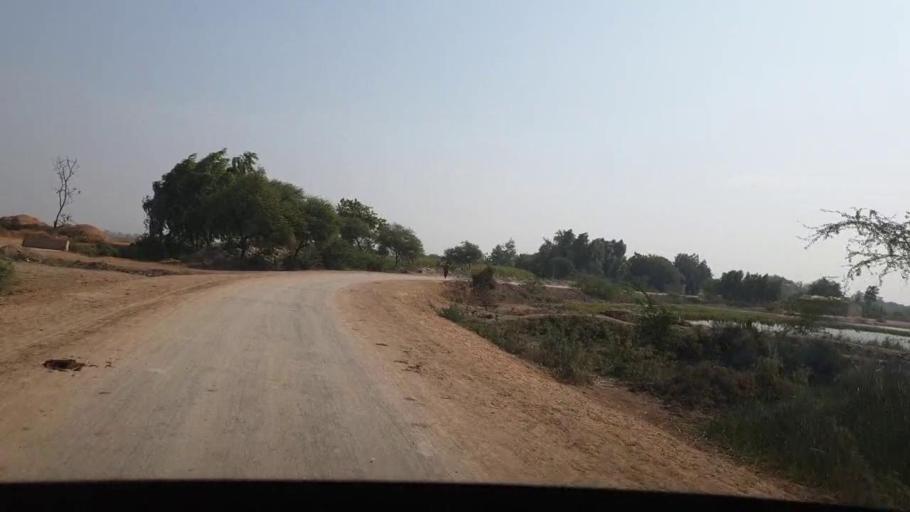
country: PK
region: Sindh
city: Chuhar Jamali
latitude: 24.2682
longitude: 67.9413
